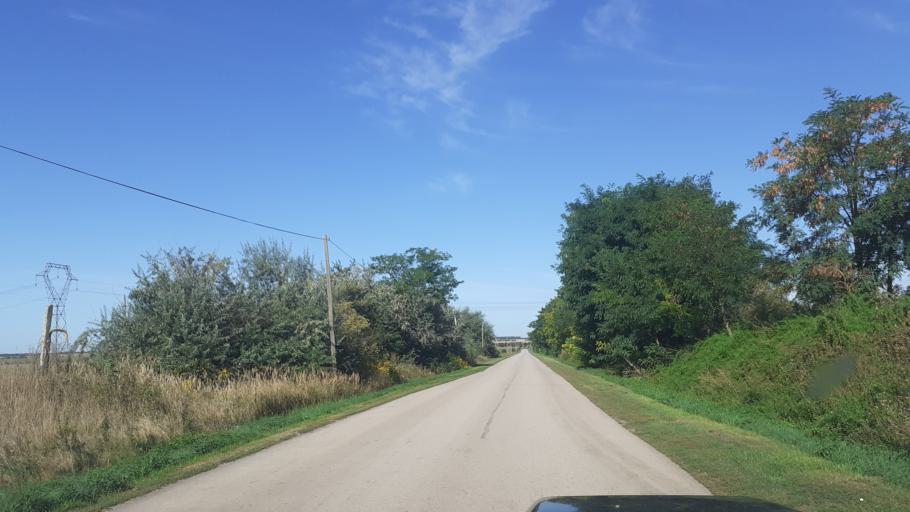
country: HU
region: Fejer
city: Pusztaszabolcs
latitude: 47.1920
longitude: 18.7713
